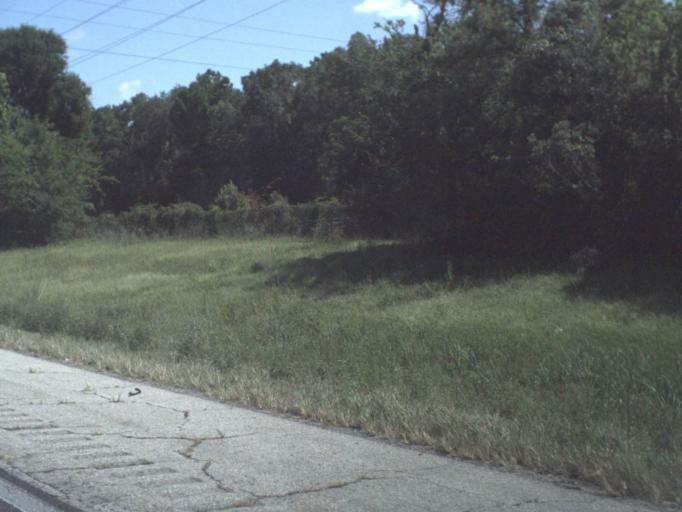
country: US
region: Florida
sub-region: Alachua County
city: Gainesville
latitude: 29.6298
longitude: -82.3947
